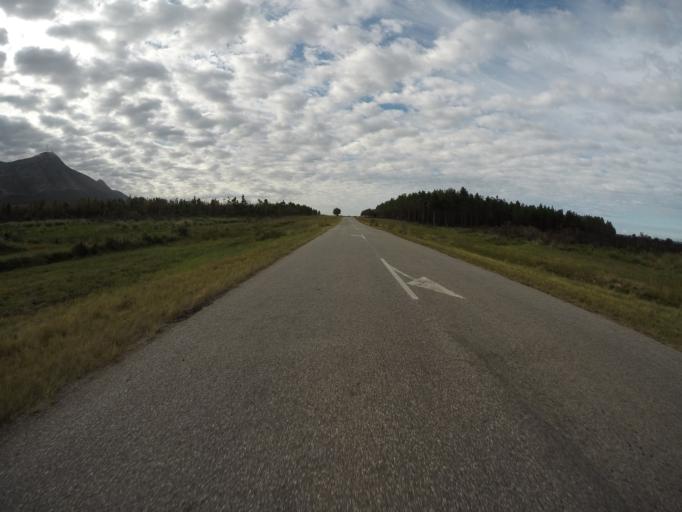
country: ZA
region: Eastern Cape
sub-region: Cacadu District Municipality
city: Kareedouw
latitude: -34.0386
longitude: 24.4017
